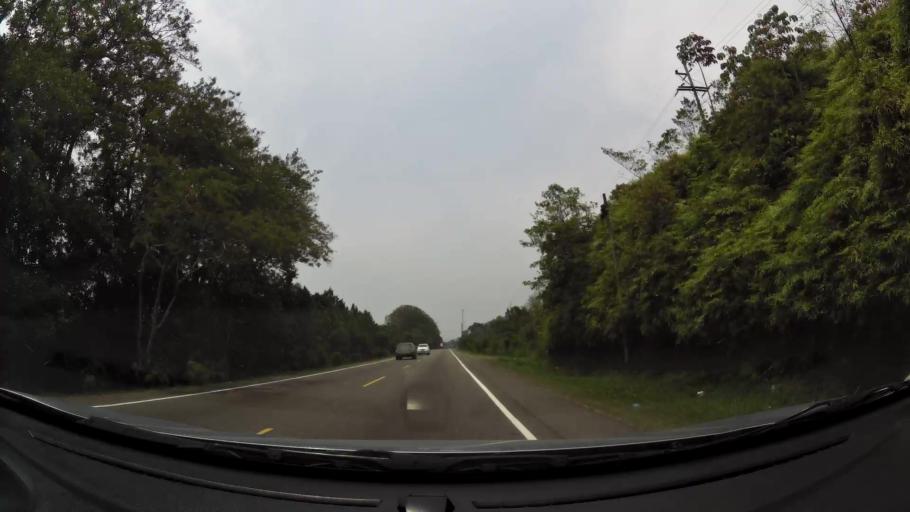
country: HN
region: Cortes
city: La Guama
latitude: 14.8355
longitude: -87.9599
